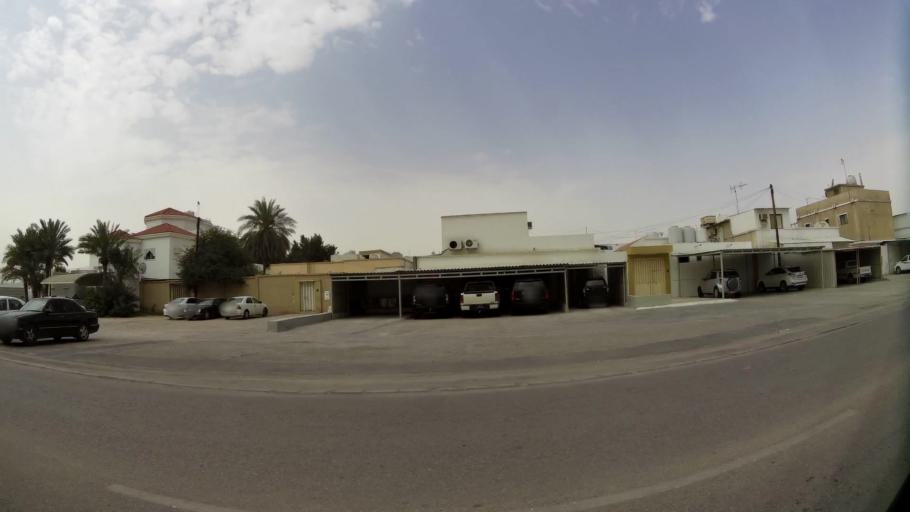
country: QA
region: Baladiyat ad Dawhah
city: Doha
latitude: 25.3047
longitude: 51.4930
